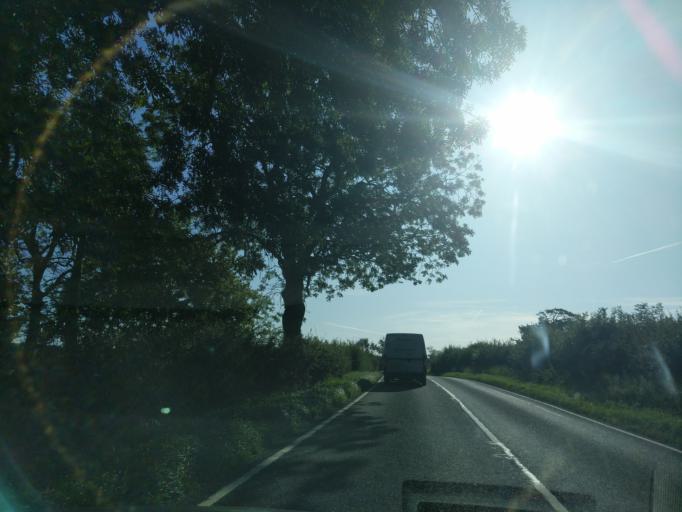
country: GB
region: England
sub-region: District of Rutland
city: Clipsham
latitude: 52.8077
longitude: -0.5014
